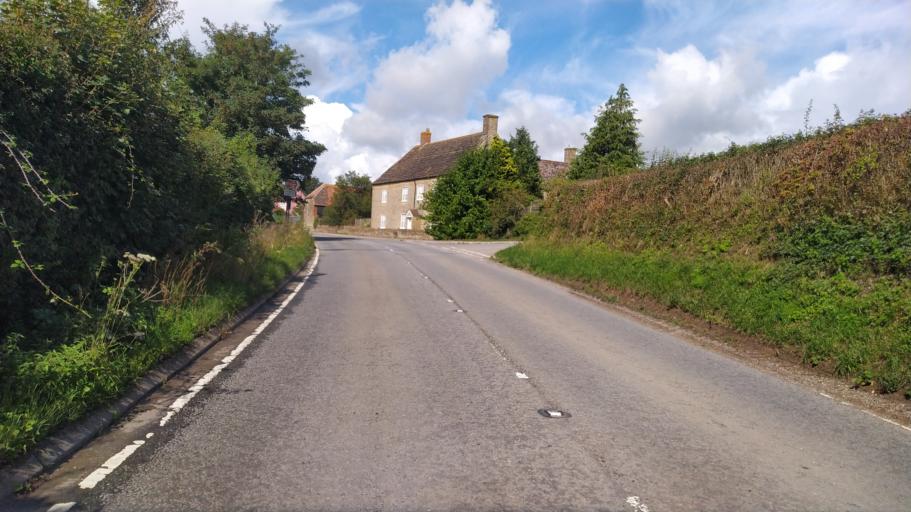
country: GB
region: England
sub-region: Somerset
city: Milborne Port
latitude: 50.9175
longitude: -2.4302
